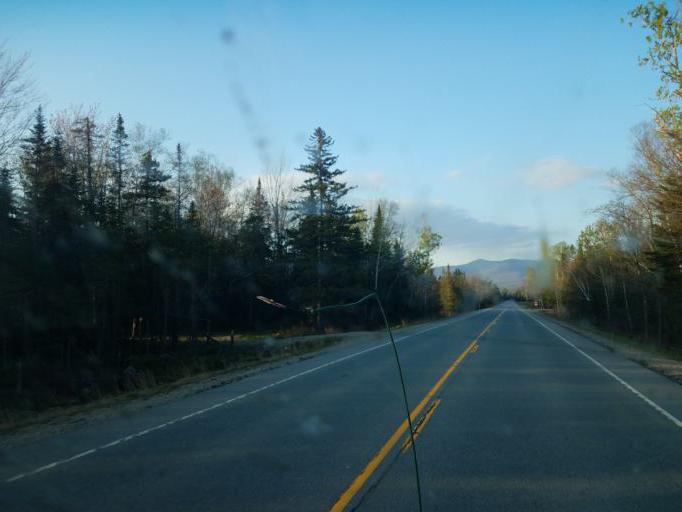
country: US
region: New Hampshire
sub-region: Grafton County
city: Deerfield
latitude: 44.2573
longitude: -71.5856
